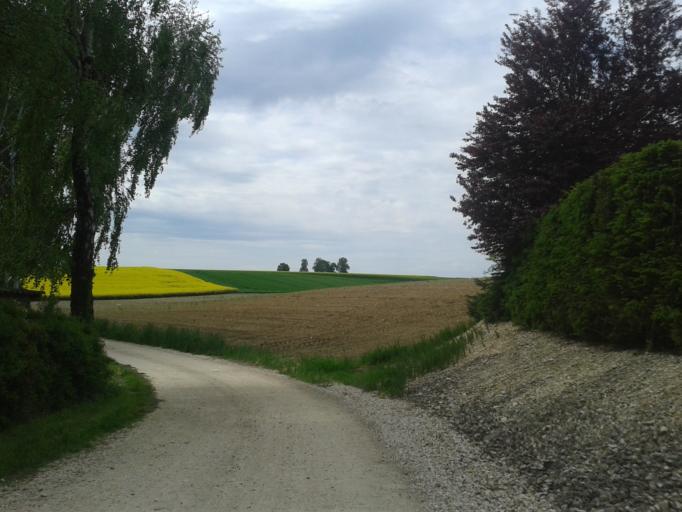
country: DE
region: Baden-Wuerttemberg
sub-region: Tuebingen Region
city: Erbach
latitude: 48.3431
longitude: 9.9013
